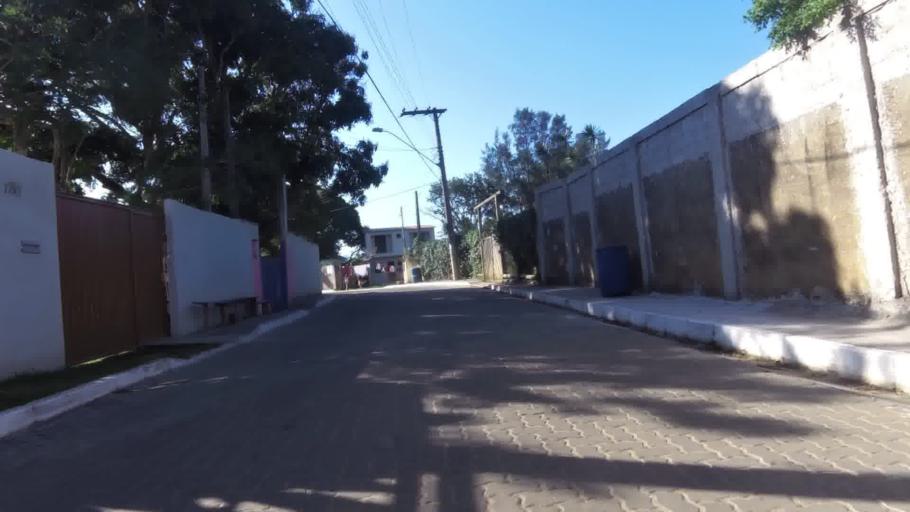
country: BR
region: Espirito Santo
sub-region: Guarapari
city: Guarapari
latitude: -20.7502
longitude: -40.5615
